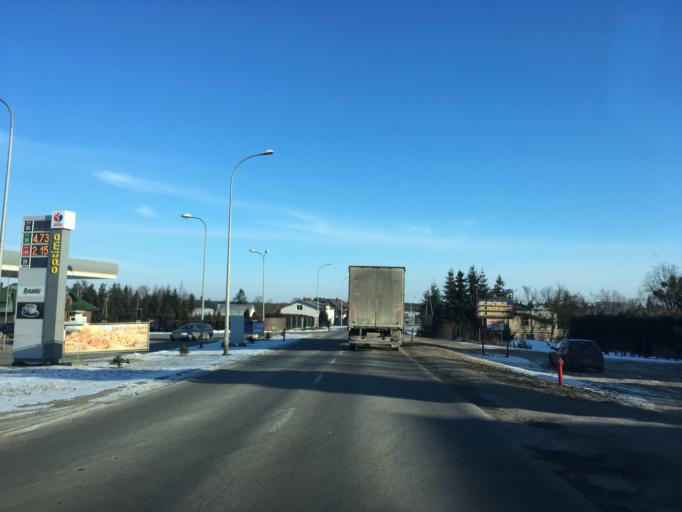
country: PL
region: Pomeranian Voivodeship
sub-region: Powiat starogardzki
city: Zblewo
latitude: 53.9411
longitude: 18.3218
